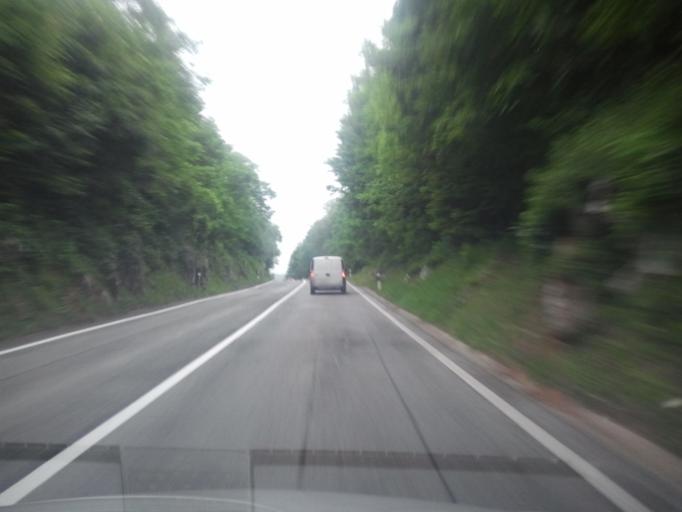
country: HR
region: Karlovacka
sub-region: Grad Karlovac
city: Slunj
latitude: 45.2174
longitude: 15.5487
